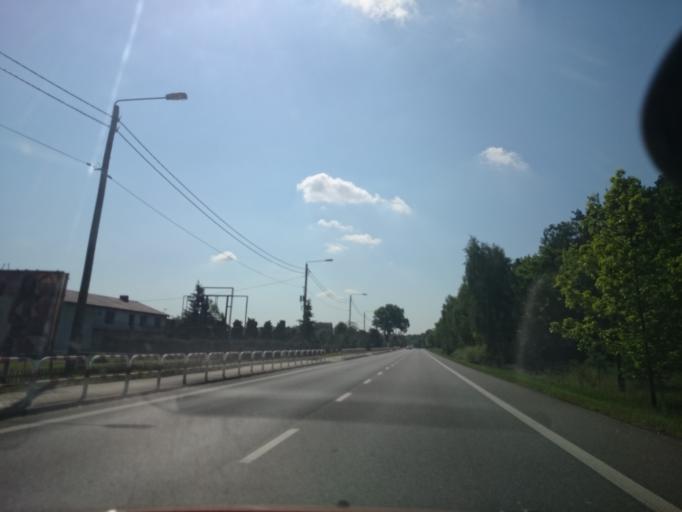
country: PL
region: Opole Voivodeship
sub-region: Powiat opolski
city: Tarnow Opolski
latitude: 50.6098
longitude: 18.0704
